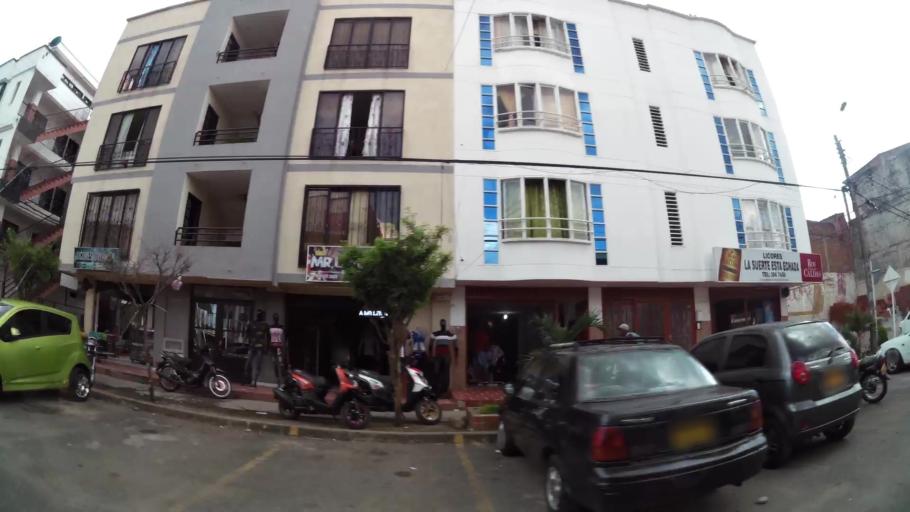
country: CO
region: Valle del Cauca
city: Cali
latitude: 3.4025
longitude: -76.5025
